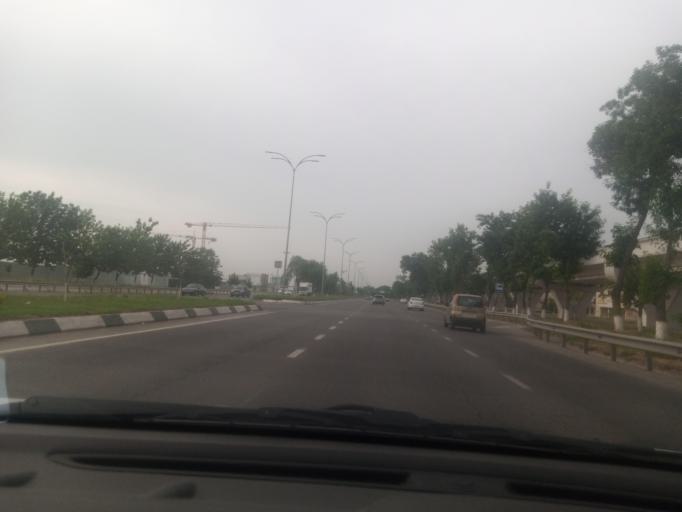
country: UZ
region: Toshkent Shahri
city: Bektemir
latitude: 41.2780
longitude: 69.3613
